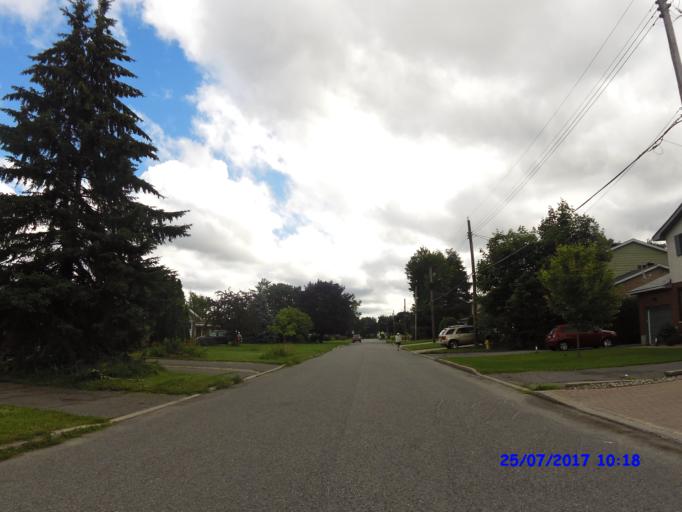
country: CA
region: Ontario
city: Ottawa
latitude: 45.3591
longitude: -75.7147
